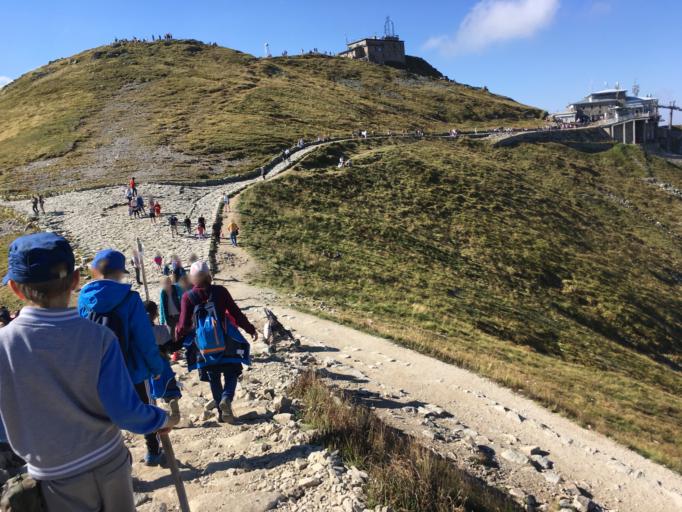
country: PL
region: Lesser Poland Voivodeship
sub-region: Powiat tatrzanski
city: Zakopane
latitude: 49.2308
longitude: 19.9834
